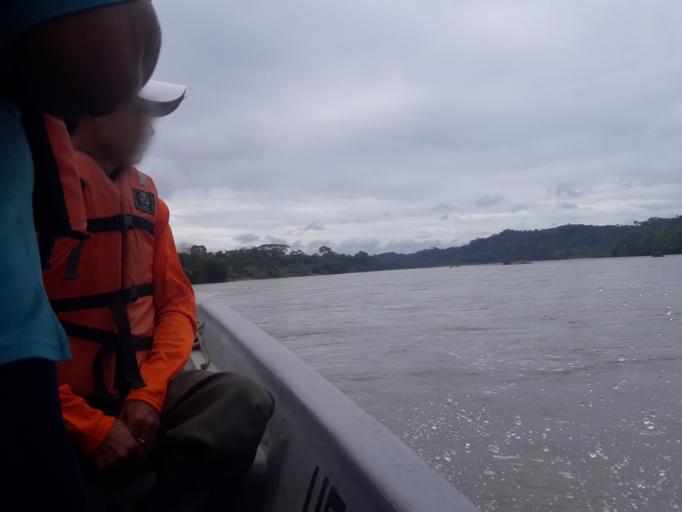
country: EC
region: Orellana
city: Boca Suno
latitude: -0.8801
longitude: -77.2918
